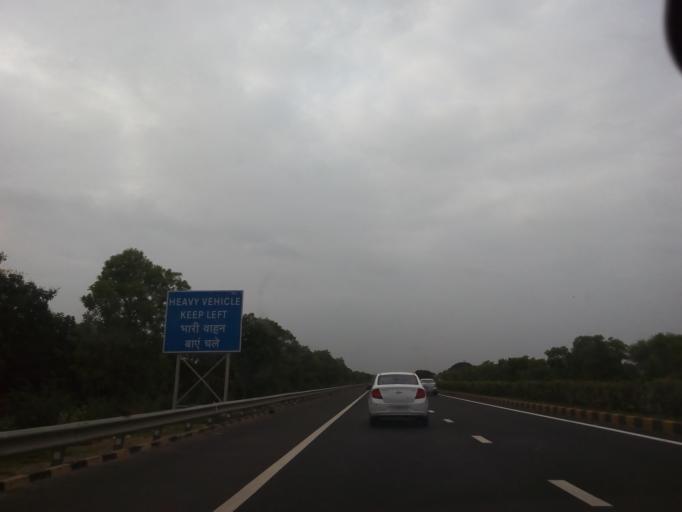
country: IN
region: Gujarat
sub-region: Kheda
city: Chaklasi
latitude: 22.6541
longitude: 72.9266
